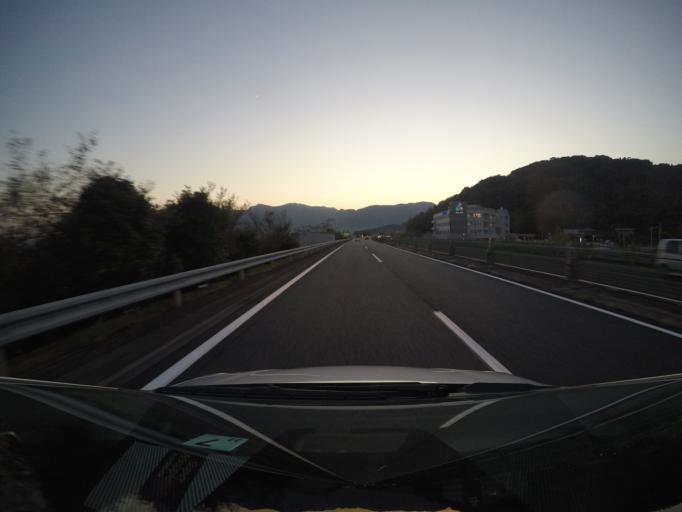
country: JP
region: Kagoshima
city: Kajiki
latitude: 31.7292
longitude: 130.6205
